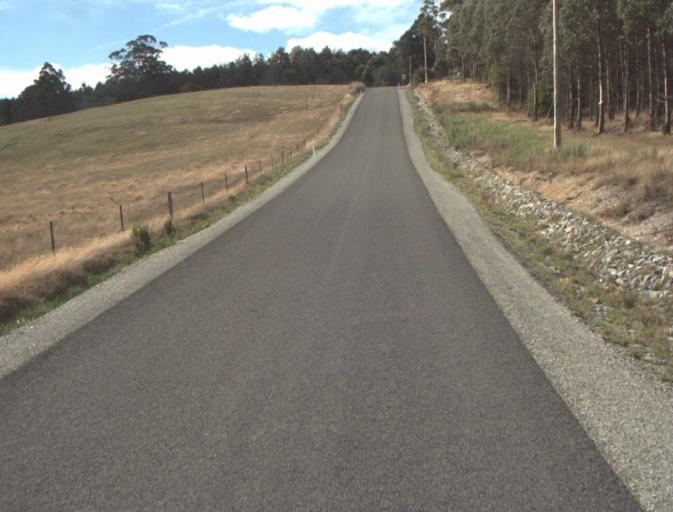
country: AU
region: Tasmania
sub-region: Launceston
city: Mayfield
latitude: -41.1957
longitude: 147.1813
